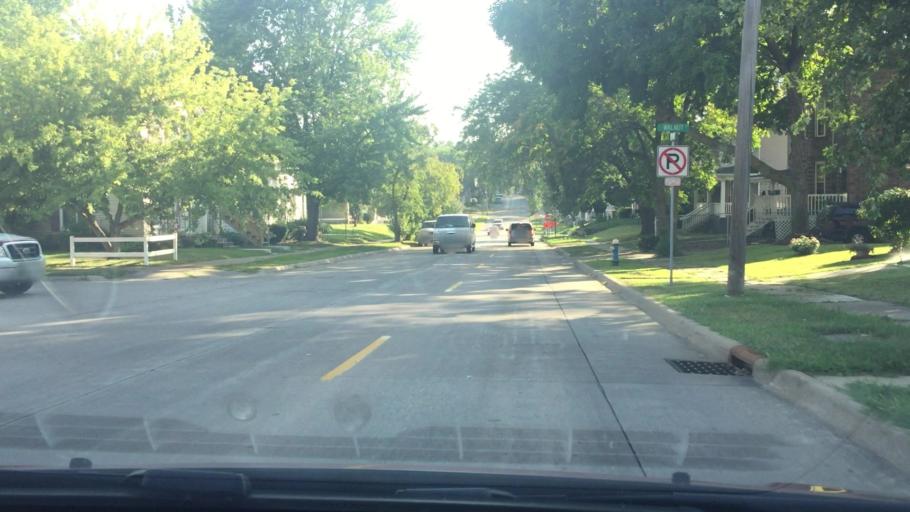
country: US
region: Iowa
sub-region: Muscatine County
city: Muscatine
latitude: 41.4280
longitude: -91.0471
